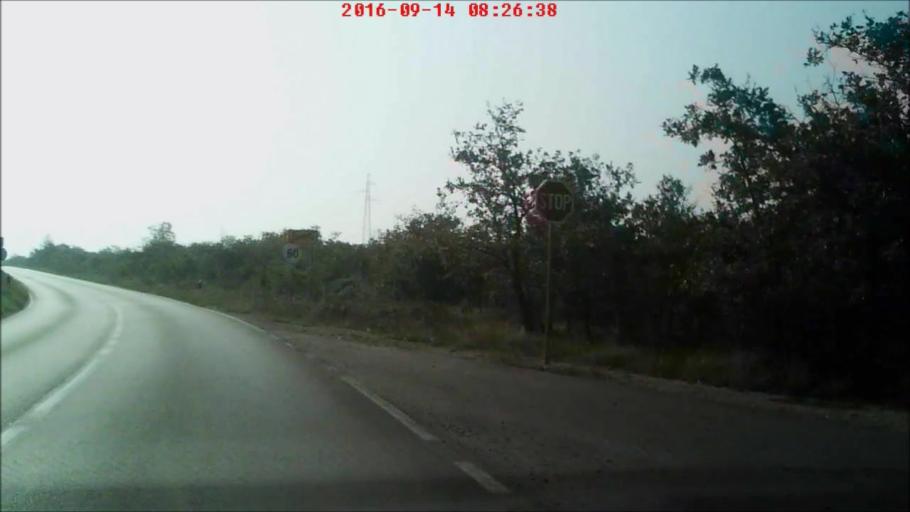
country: HR
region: Zadarska
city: Vrsi
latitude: 44.1942
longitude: 15.2564
